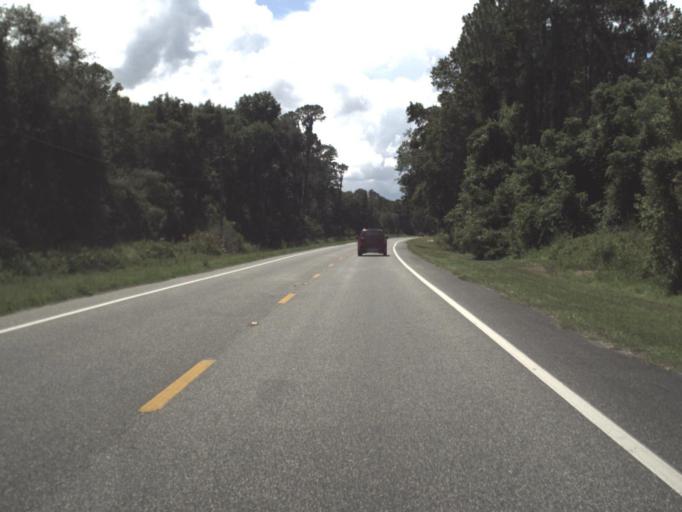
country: US
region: Florida
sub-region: Putnam County
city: Crescent City
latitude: 29.4717
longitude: -81.5322
